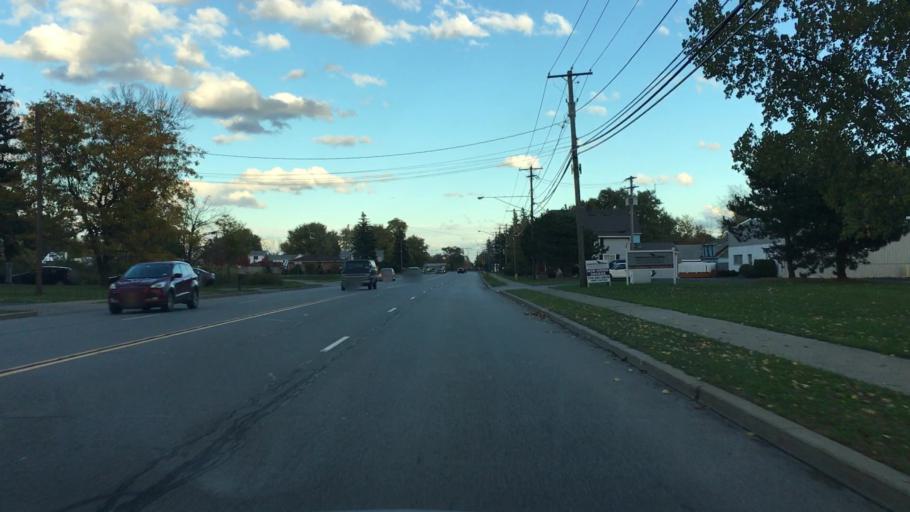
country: US
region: New York
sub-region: Erie County
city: Cheektowaga
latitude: 42.9039
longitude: -78.7377
